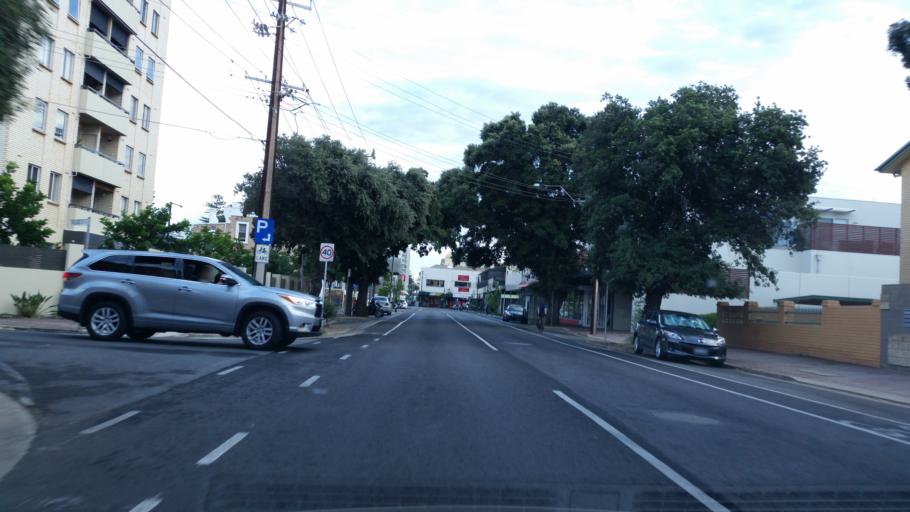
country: AU
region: South Australia
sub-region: Adelaide
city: Glenelg
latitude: -34.9818
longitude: 138.5132
